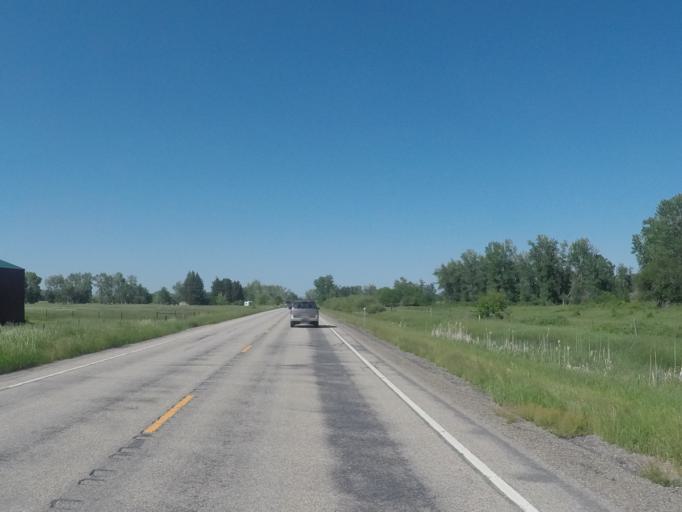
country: US
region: Montana
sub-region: Carbon County
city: Red Lodge
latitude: 45.3364
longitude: -109.1827
